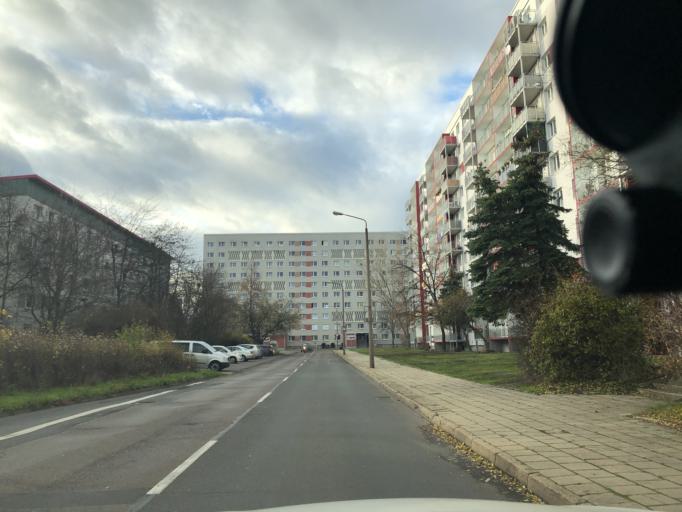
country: DE
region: Saxony-Anhalt
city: Halle Neustadt
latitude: 51.4739
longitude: 11.9129
